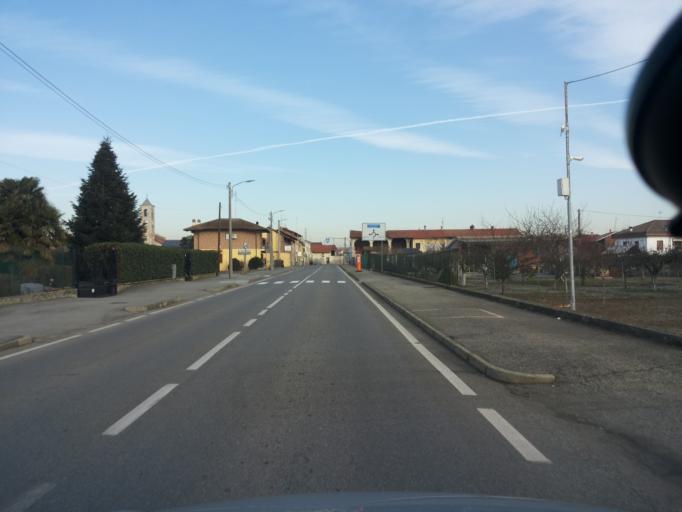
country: IT
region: Piedmont
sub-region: Provincia di Vercelli
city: Greggio
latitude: 45.4493
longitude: 8.3849
